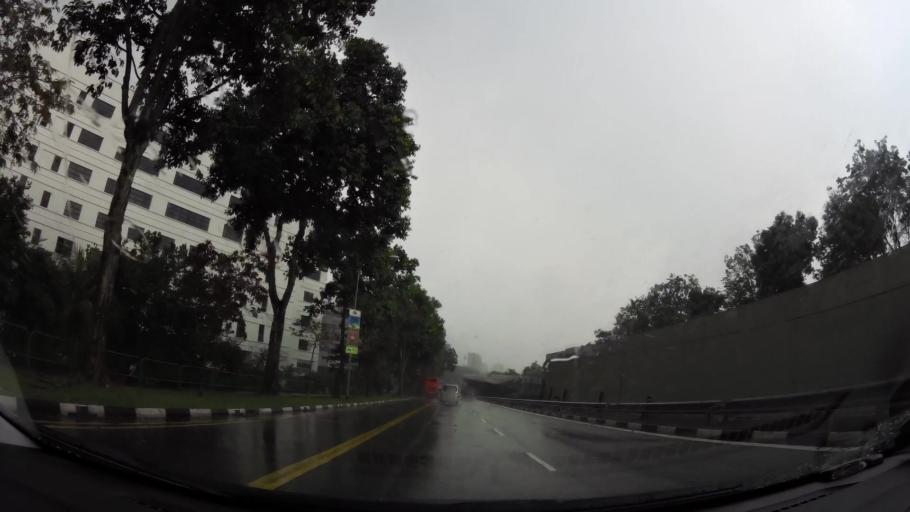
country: SG
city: Singapore
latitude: 1.3219
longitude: 103.9207
